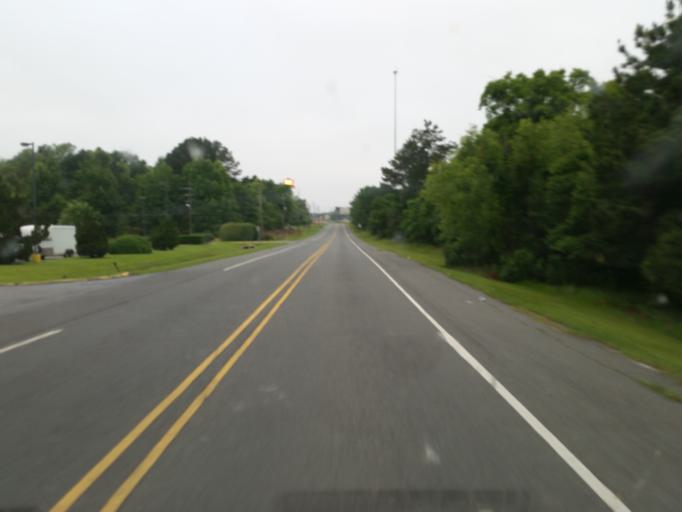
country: US
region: Louisiana
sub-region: Caddo Parish
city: Shreveport
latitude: 32.4539
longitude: -93.8471
